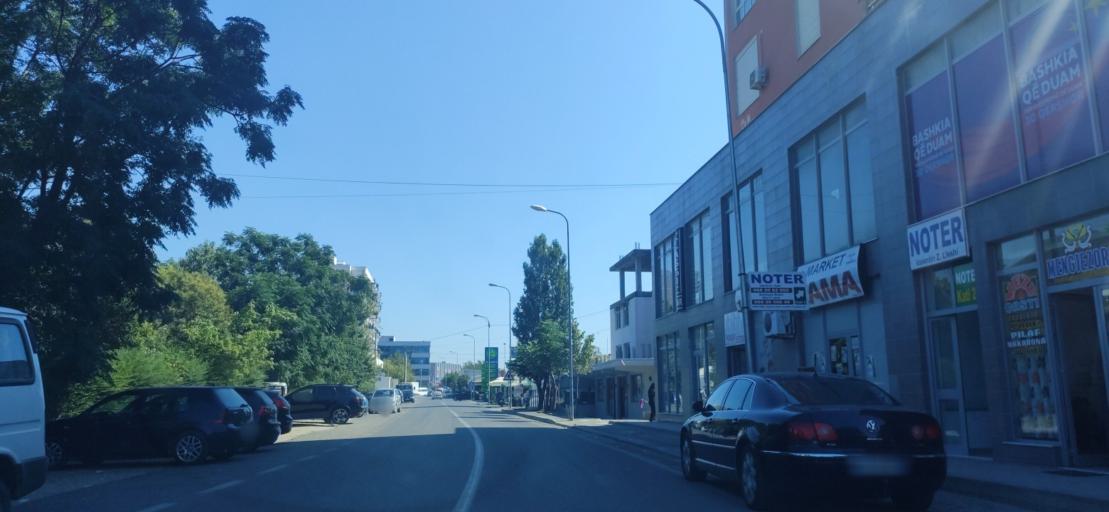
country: AL
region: Lezhe
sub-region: Rrethi i Kurbinit
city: Lac
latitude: 41.6375
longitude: 19.7114
